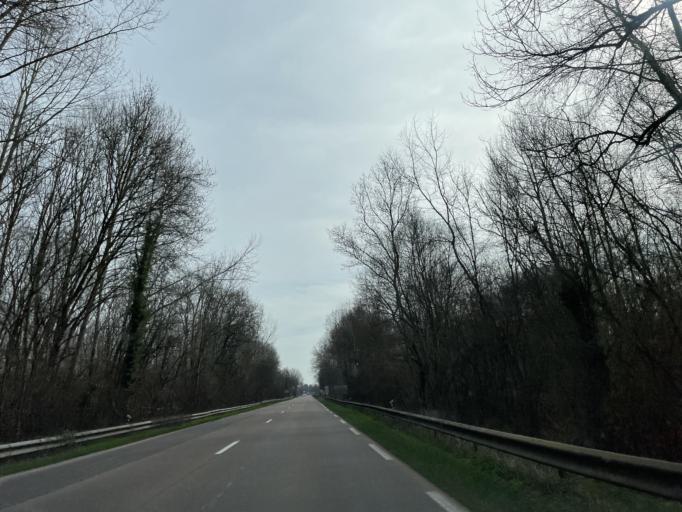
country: FR
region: Champagne-Ardenne
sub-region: Departement de l'Aube
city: Nogent-sur-Seine
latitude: 48.5038
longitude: 3.4539
